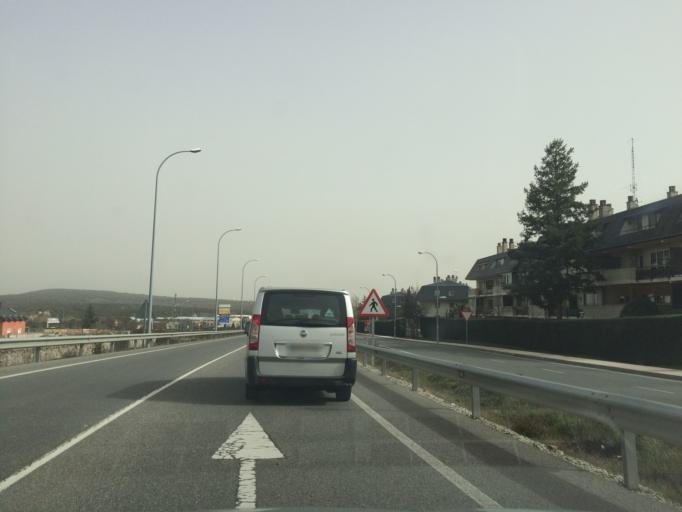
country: ES
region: Madrid
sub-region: Provincia de Madrid
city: Boalo
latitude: 40.7000
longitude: -3.9343
